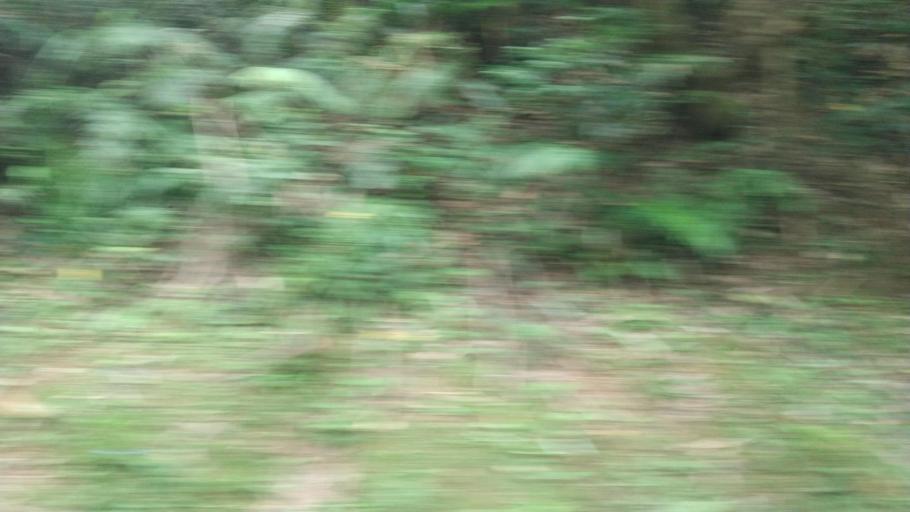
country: TW
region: Taiwan
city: Daxi
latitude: 24.9074
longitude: 121.4017
